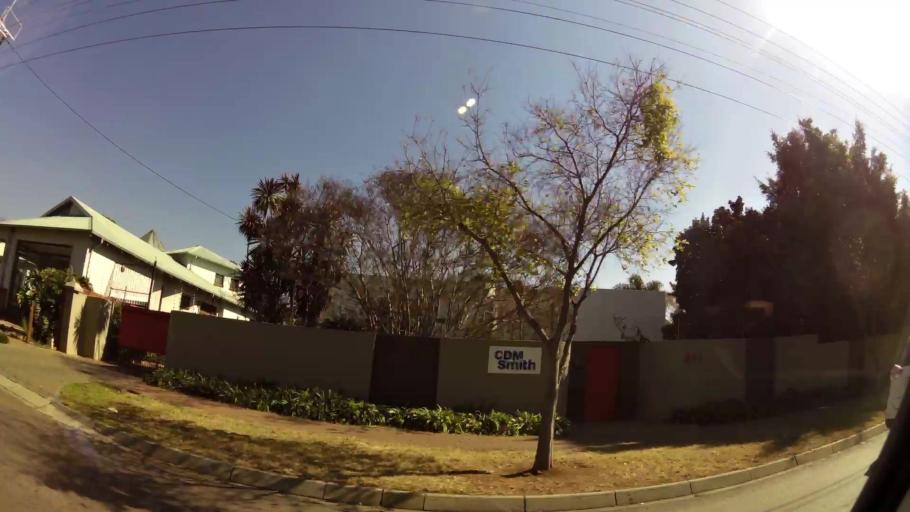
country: ZA
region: Gauteng
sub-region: City of Tshwane Metropolitan Municipality
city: Pretoria
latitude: -25.7620
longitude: 28.2375
